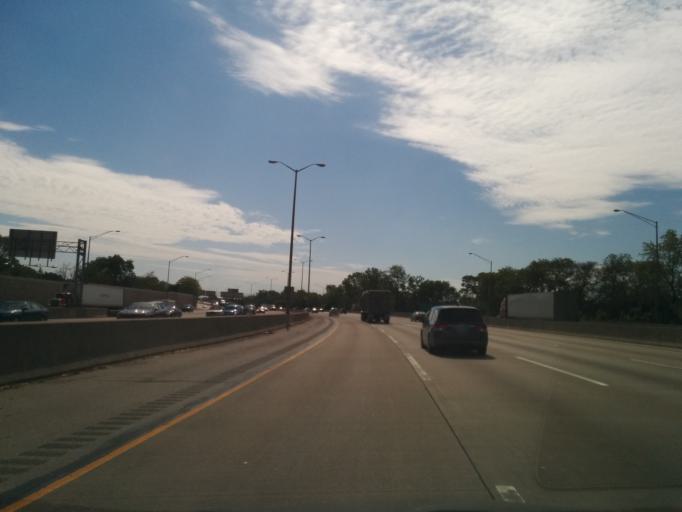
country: US
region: Illinois
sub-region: Cook County
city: University Park
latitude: 41.5787
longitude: -87.6749
